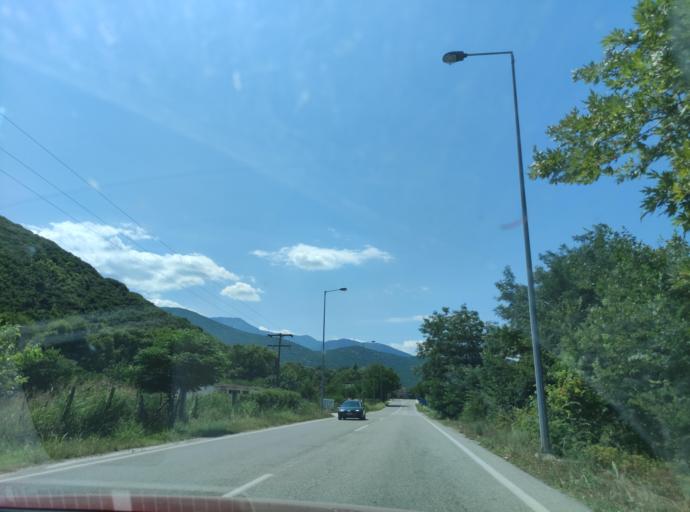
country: GR
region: East Macedonia and Thrace
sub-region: Nomos Kavalas
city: Palaiochori
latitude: 40.9526
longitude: 24.1981
